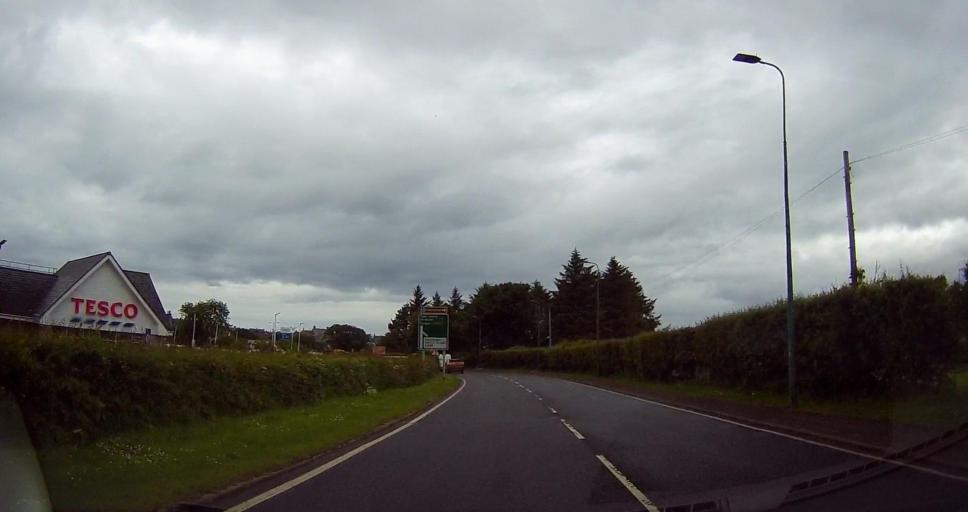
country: GB
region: Scotland
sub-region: Highland
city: Thurso
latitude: 58.5901
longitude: -3.5167
